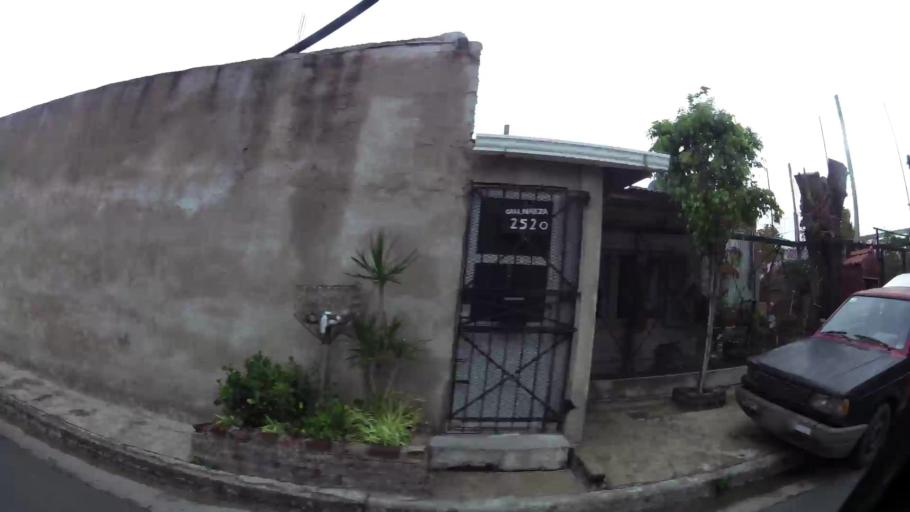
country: AR
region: Buenos Aires
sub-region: Partido de Lanus
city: Lanus
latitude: -34.7229
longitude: -58.3800
